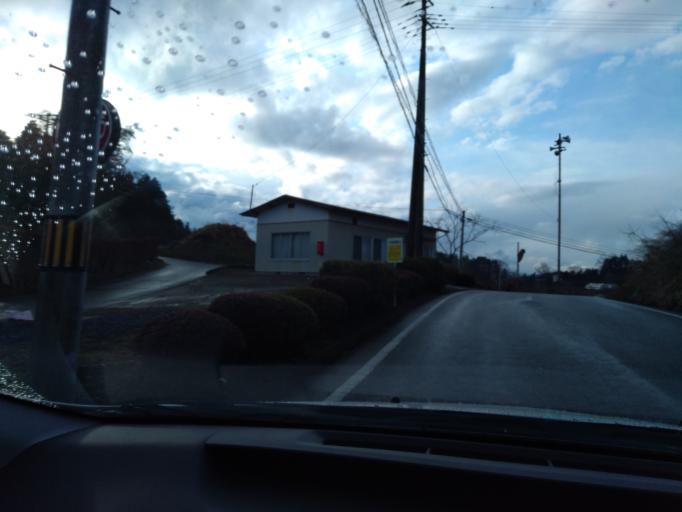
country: JP
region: Iwate
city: Ichinoseki
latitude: 38.7398
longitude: 141.1211
